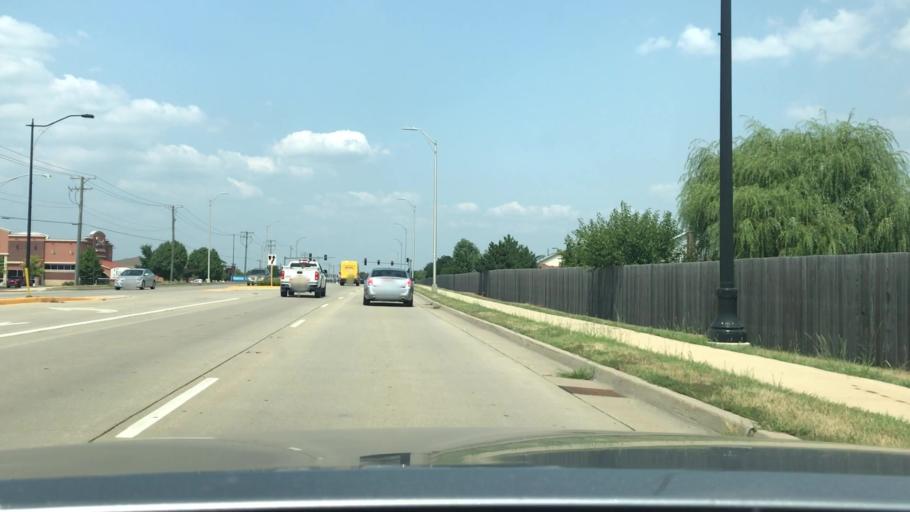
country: US
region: Illinois
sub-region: Will County
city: Shorewood
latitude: 41.5449
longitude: -88.1994
